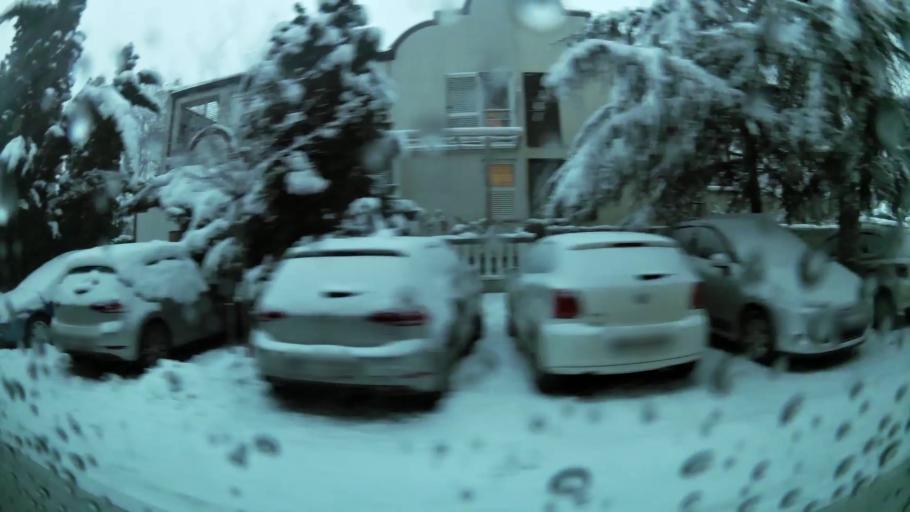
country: RS
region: Central Serbia
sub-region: Belgrade
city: Zemun
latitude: 44.8152
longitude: 20.3858
